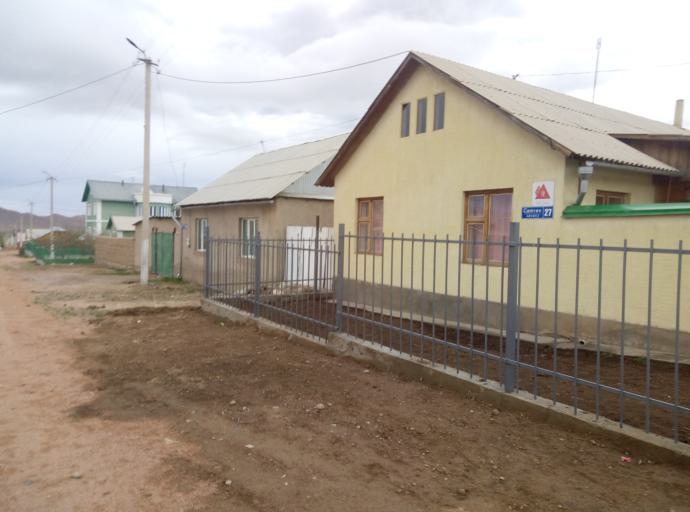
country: KG
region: Ysyk-Koel
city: Bokombayevskoye
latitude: 42.1119
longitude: 76.9793
